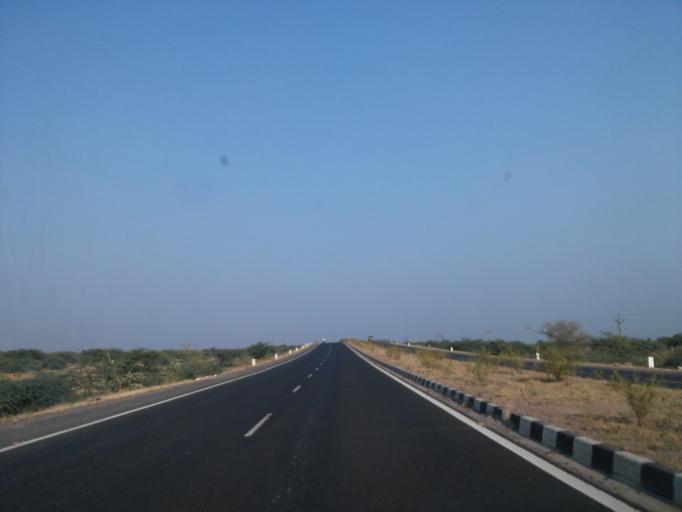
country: IN
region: Gujarat
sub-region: Surendranagar
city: Dhrangadhra
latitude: 23.0262
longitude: 71.6427
